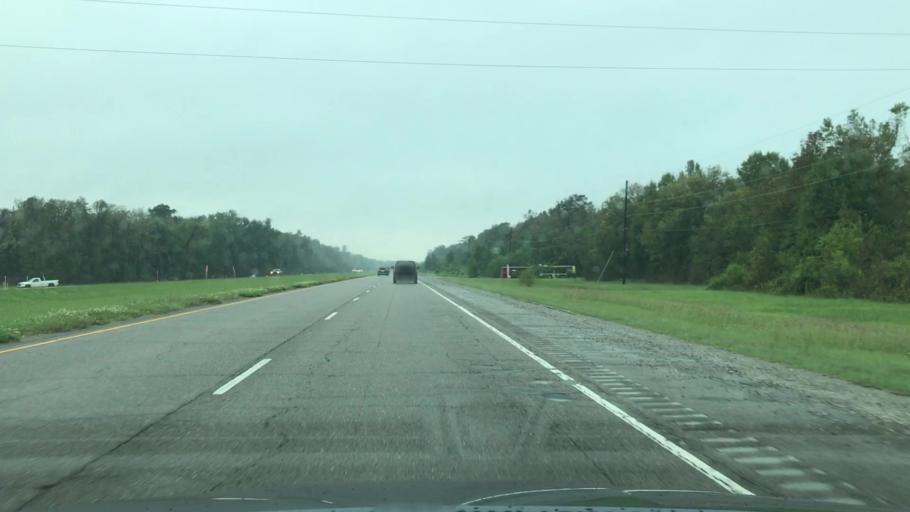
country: US
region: Louisiana
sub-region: Lafourche Parish
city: Raceland
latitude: 29.7371
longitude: -90.5577
